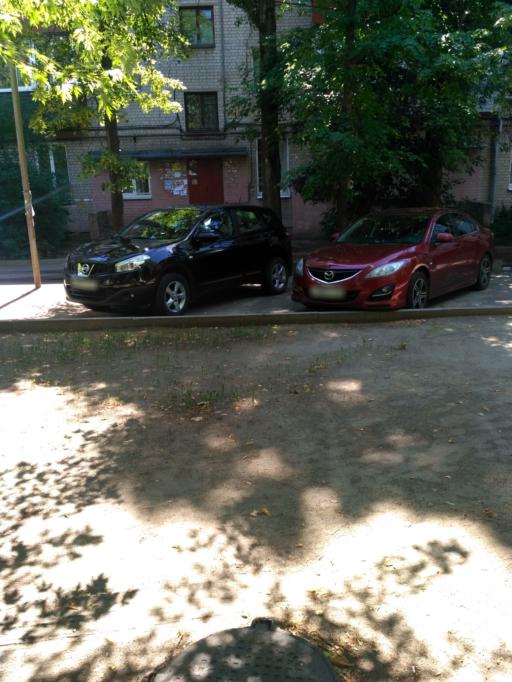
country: RU
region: Voronezj
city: Voronezh
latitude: 51.6461
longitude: 39.1502
